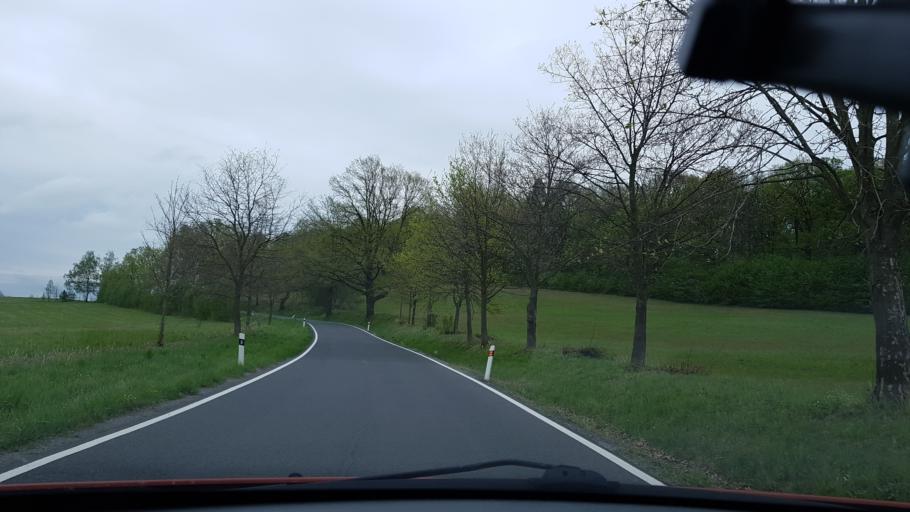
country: CZ
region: Olomoucky
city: Vidnava
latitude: 50.3856
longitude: 17.1239
